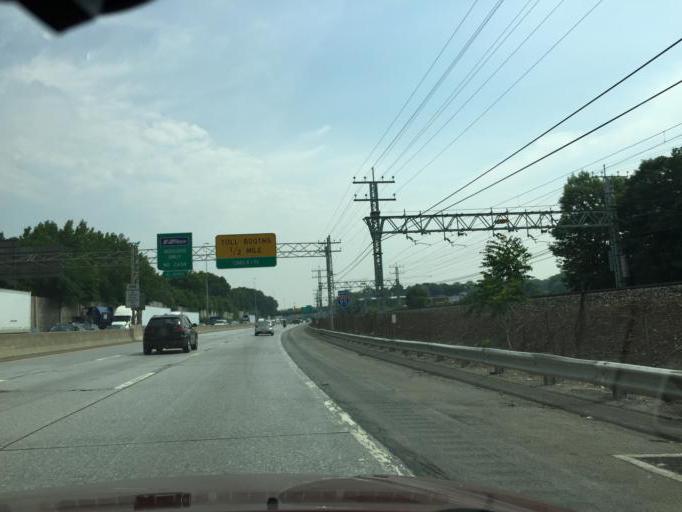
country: US
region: New York
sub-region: Westchester County
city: New Rochelle
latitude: 40.9212
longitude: -73.7765
